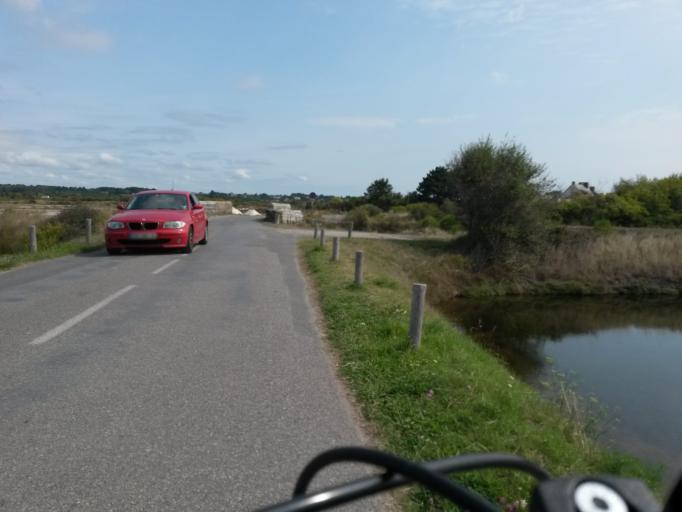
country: FR
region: Pays de la Loire
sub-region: Departement de la Loire-Atlantique
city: La Turballe
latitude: 47.3219
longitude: -2.4882
